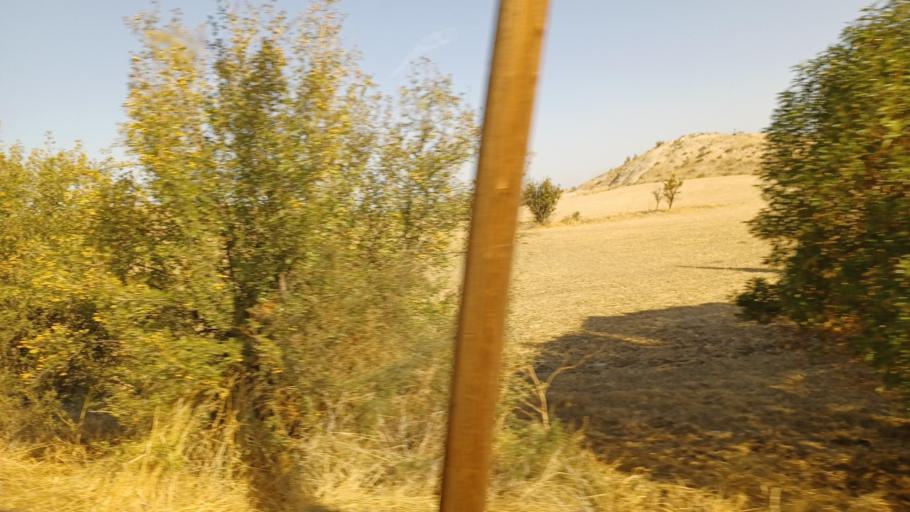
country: CY
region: Lefkosia
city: Alampra
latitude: 34.9827
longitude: 33.3525
